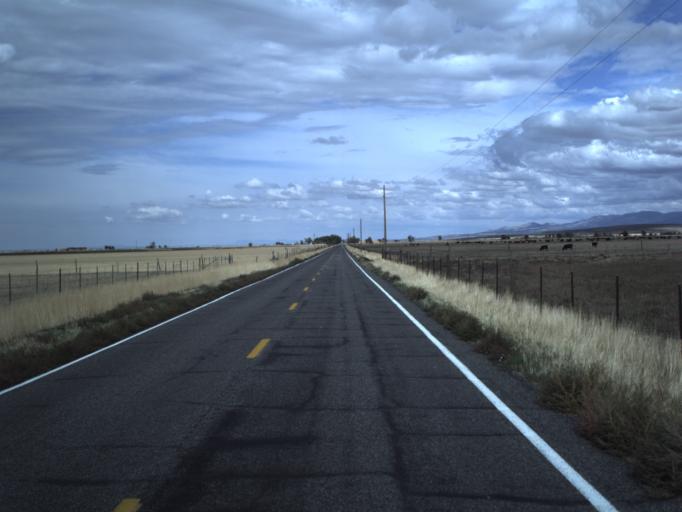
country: US
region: Utah
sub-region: Millard County
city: Fillmore
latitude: 39.0260
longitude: -112.4100
